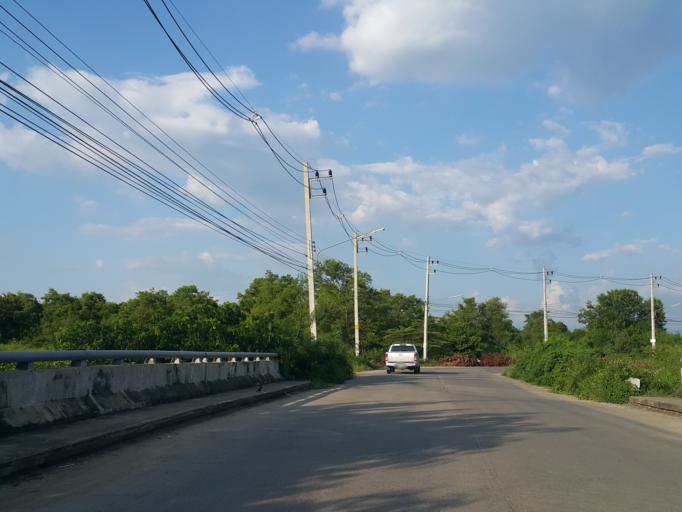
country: TH
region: Chiang Mai
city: San Kamphaeng
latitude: 18.7421
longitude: 99.0825
